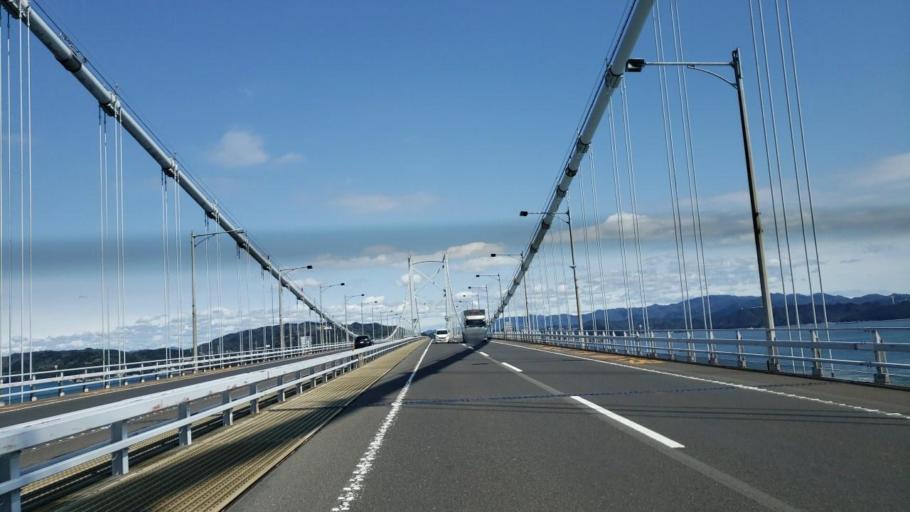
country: JP
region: Tokushima
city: Narutocho-mitsuishi
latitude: 34.2382
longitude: 134.6472
